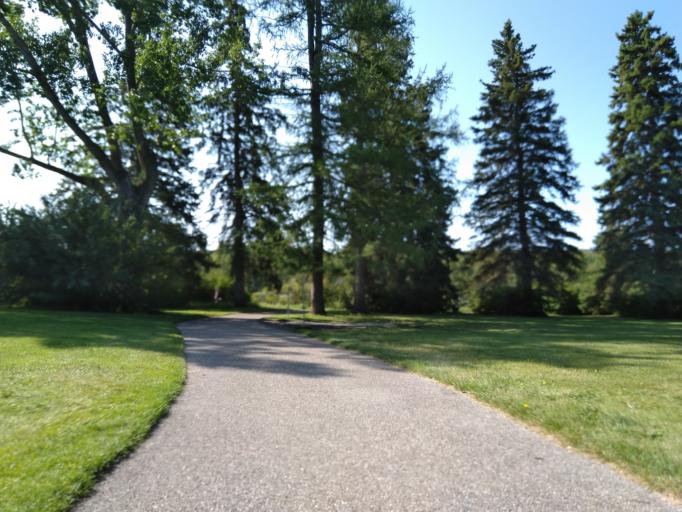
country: CA
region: Alberta
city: Calgary
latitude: 51.1002
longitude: -114.2205
